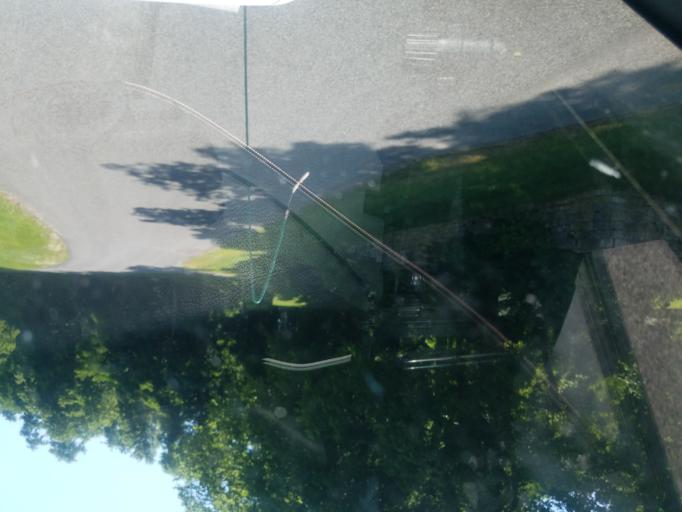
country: US
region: Ohio
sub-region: Logan County
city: West Liberty
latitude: 40.2496
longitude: -83.7289
